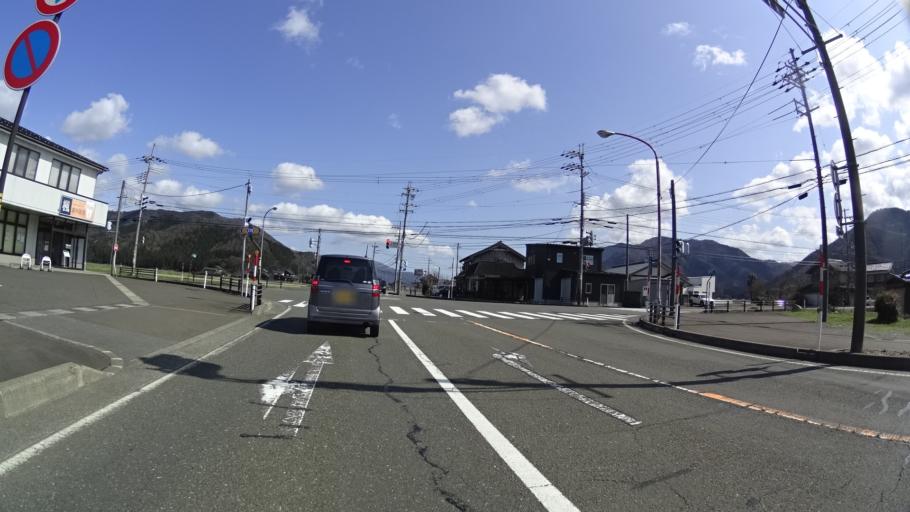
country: JP
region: Fukui
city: Obama
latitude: 35.4793
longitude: 135.8144
